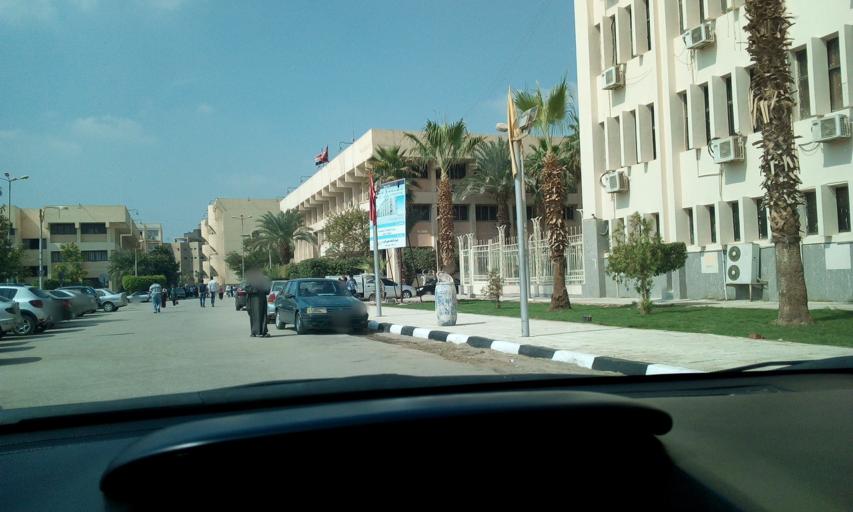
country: EG
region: Muhafazat al Fayyum
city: Al Fayyum
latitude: 29.3209
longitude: 30.8343
